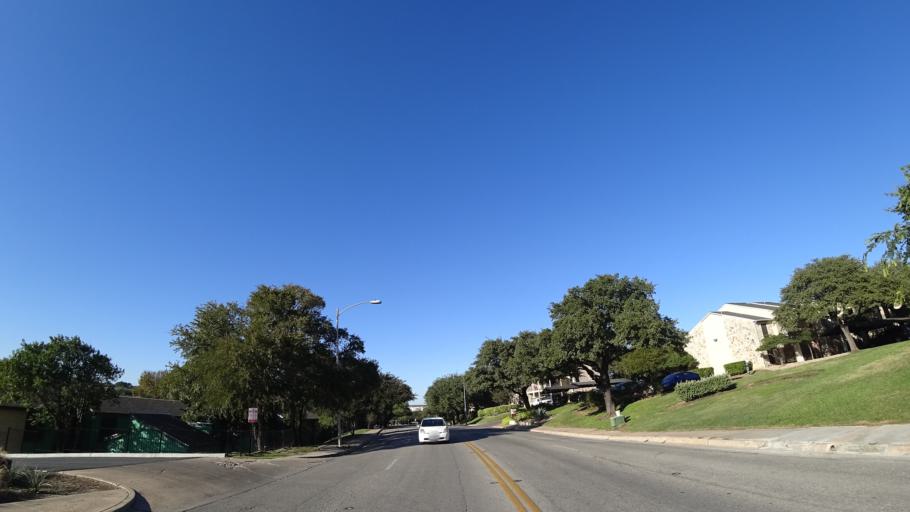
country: US
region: Texas
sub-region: Travis County
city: Austin
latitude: 30.2280
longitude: -97.7215
